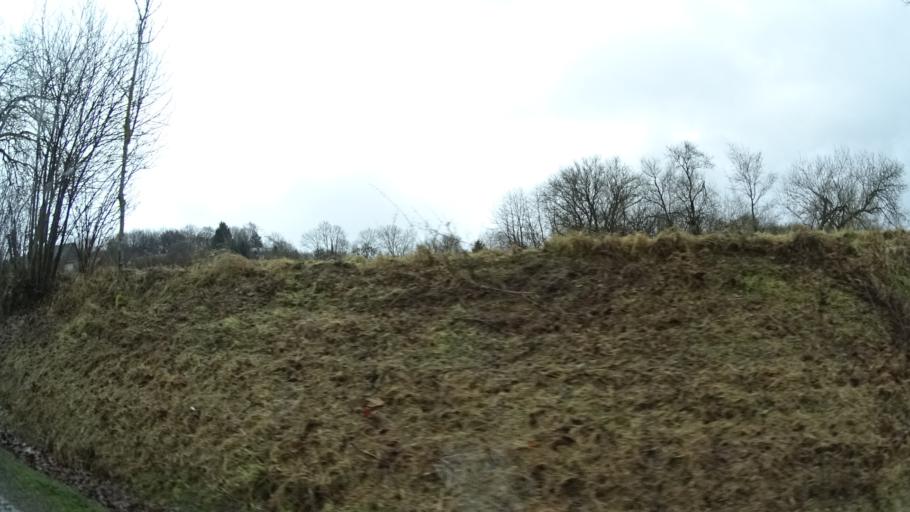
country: DE
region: Hesse
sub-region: Regierungsbezirk Giessen
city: Ulrichstein
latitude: 50.5801
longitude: 9.1862
